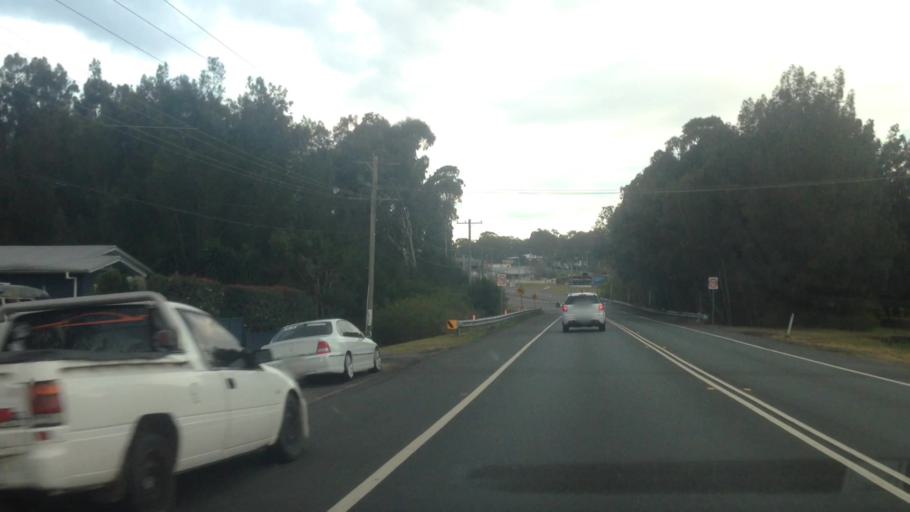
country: AU
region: New South Wales
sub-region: Wyong Shire
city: Kanwal
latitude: -33.2635
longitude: 151.4779
